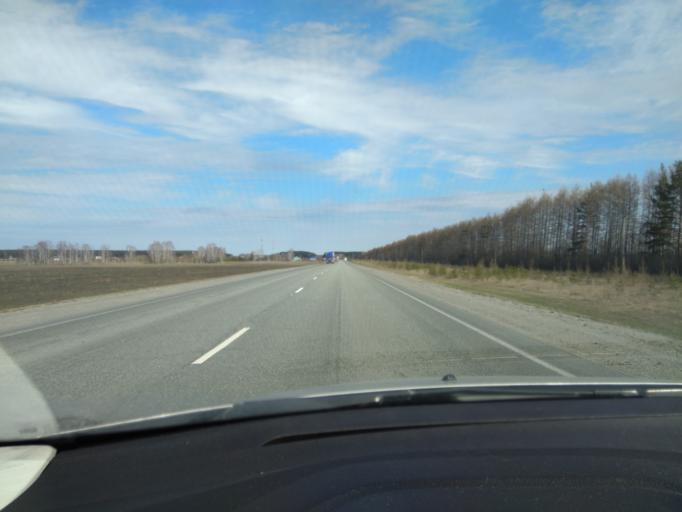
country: RU
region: Sverdlovsk
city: Troitskiy
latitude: 57.0863
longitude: 63.7164
